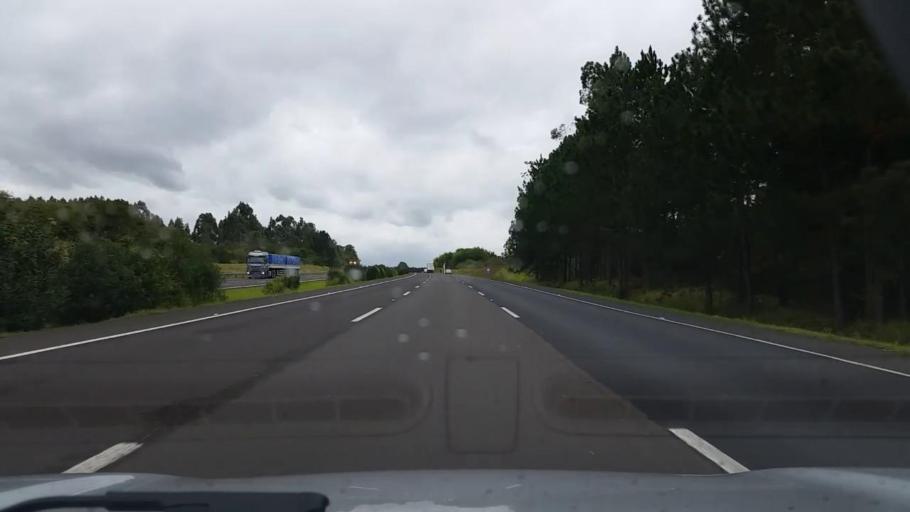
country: BR
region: Rio Grande do Sul
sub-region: Gravatai
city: Gravatai
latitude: -29.9232
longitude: -50.8528
